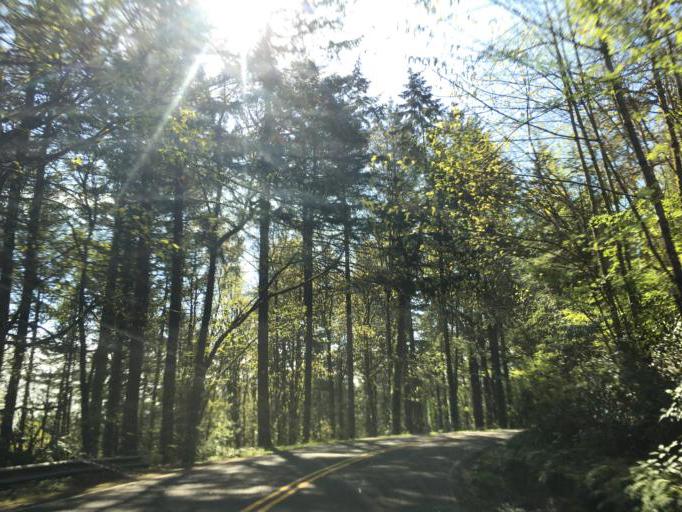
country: US
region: Oregon
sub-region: Multnomah County
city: Portland
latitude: 45.5140
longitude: -122.7094
